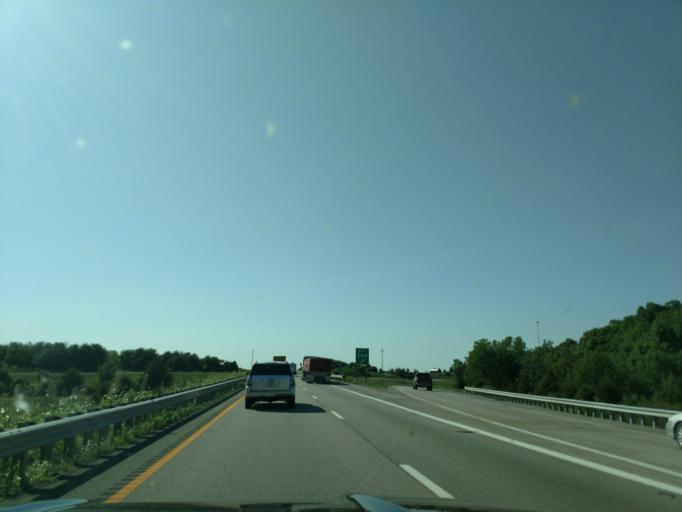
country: US
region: Missouri
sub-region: Andrew County
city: Savannah
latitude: 39.8853
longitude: -94.8546
